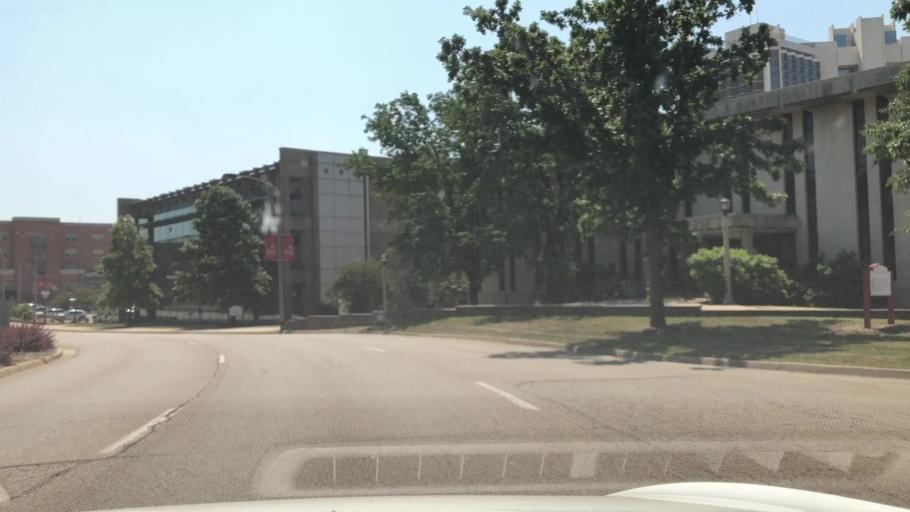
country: US
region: Illinois
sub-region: McLean County
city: Normal
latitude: 40.5104
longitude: -88.9893
